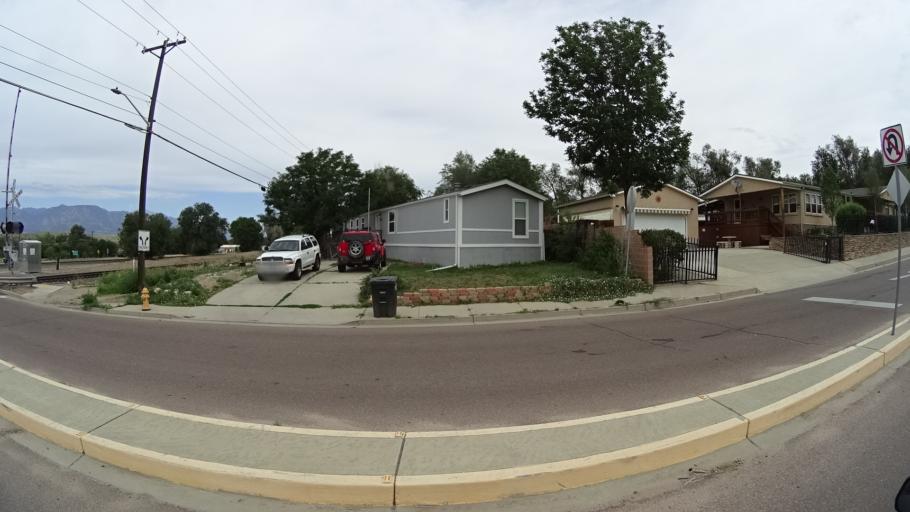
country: US
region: Colorado
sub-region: El Paso County
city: Fountain
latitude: 38.6969
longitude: -104.7041
